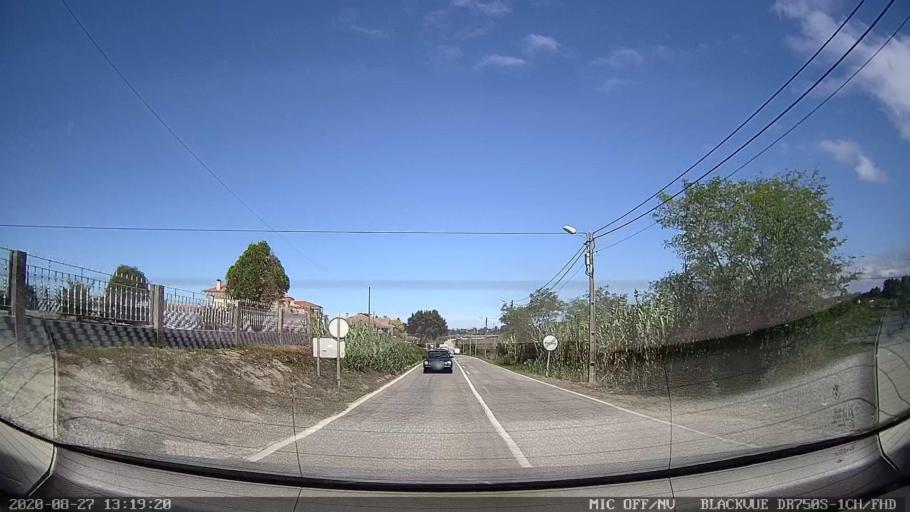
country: PT
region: Aveiro
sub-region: Vagos
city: Vagos
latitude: 40.5649
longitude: -8.6825
